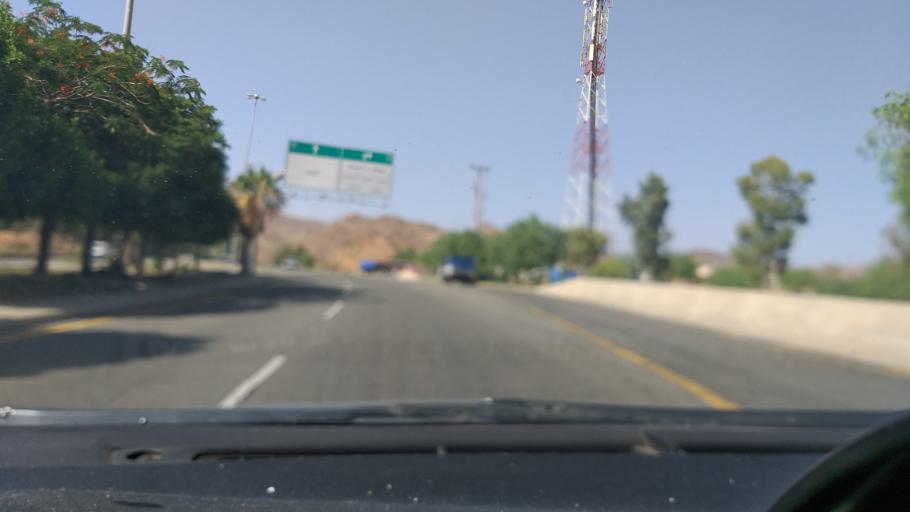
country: SA
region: Makkah
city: Ash Shafa
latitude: 21.1597
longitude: 40.3704
